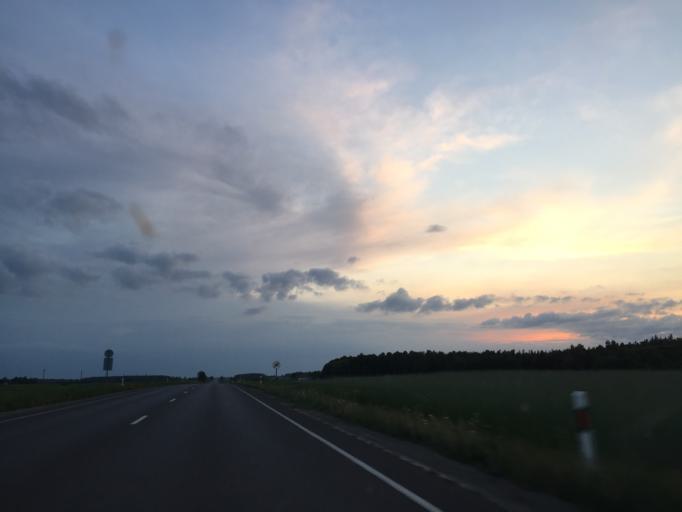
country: LT
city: Vieksniai
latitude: 55.9981
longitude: 22.4933
